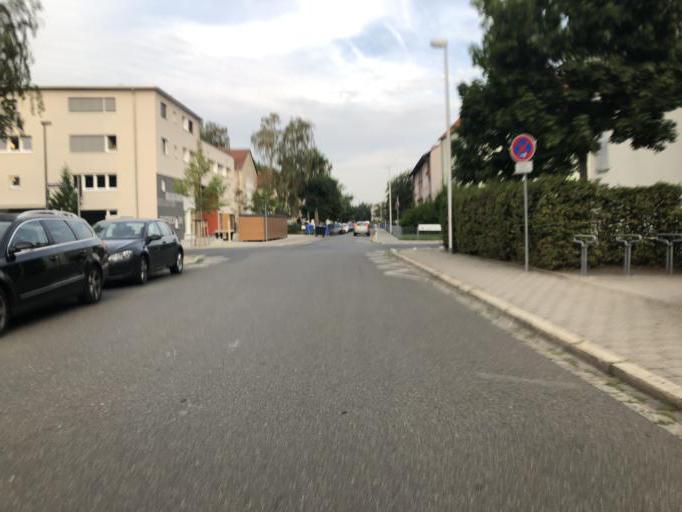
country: DE
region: Bavaria
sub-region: Regierungsbezirk Mittelfranken
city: Erlangen
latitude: 49.5845
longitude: 10.9982
